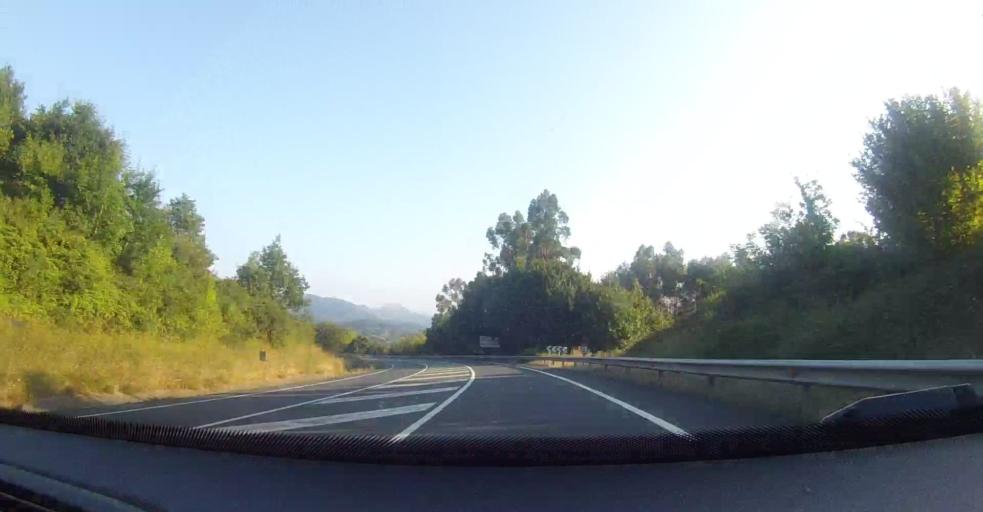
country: ES
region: Cantabria
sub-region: Provincia de Cantabria
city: Limpias
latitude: 43.3592
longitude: -3.4179
